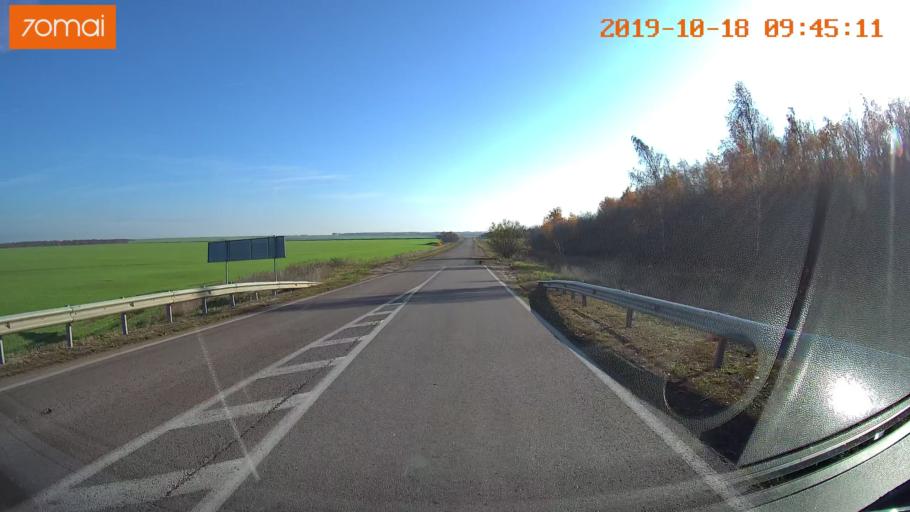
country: RU
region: Tula
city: Kazachka
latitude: 53.3124
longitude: 38.1850
